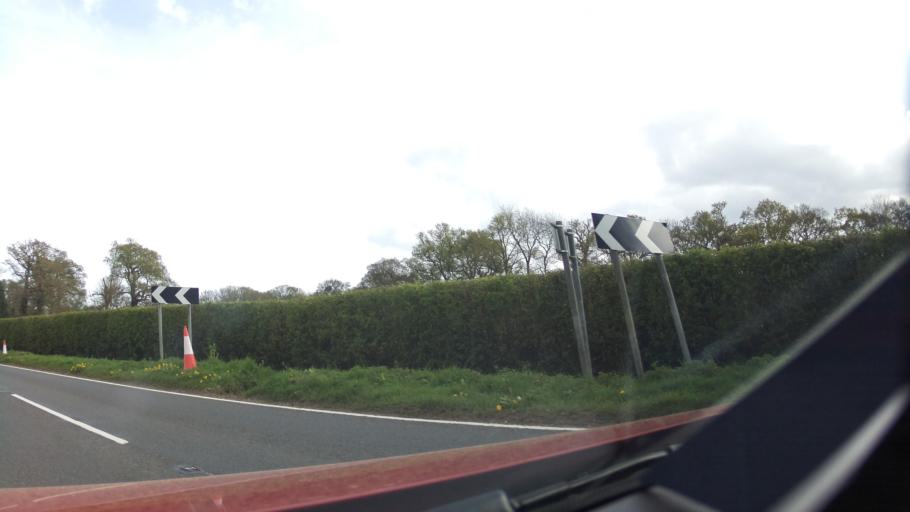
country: GB
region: England
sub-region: Hampshire
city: Chandlers Ford
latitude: 51.0197
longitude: -1.3843
